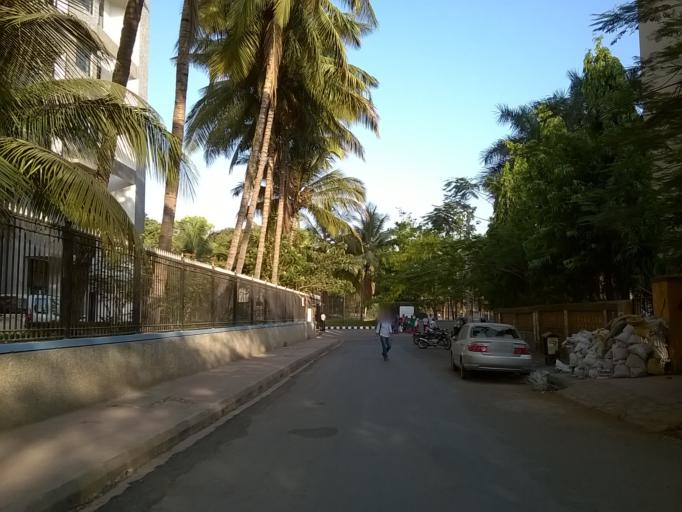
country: IN
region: Maharashtra
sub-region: Raigarh
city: Kalundri
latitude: 18.9901
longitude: 73.1275
